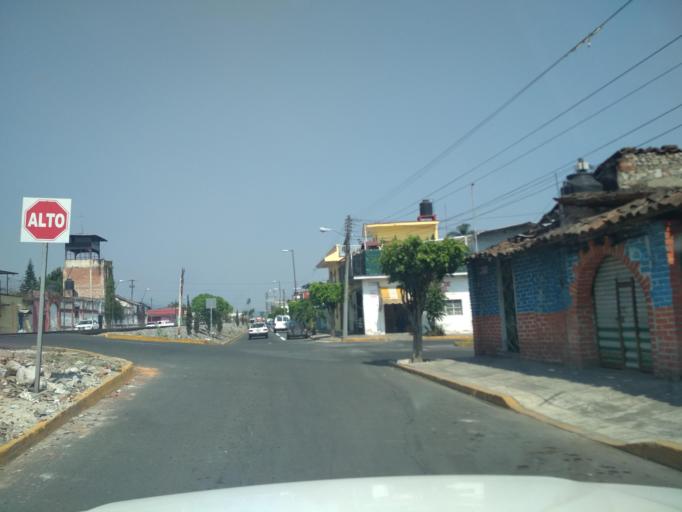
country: MX
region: Veracruz
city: Orizaba
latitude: 18.8434
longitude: -97.0957
